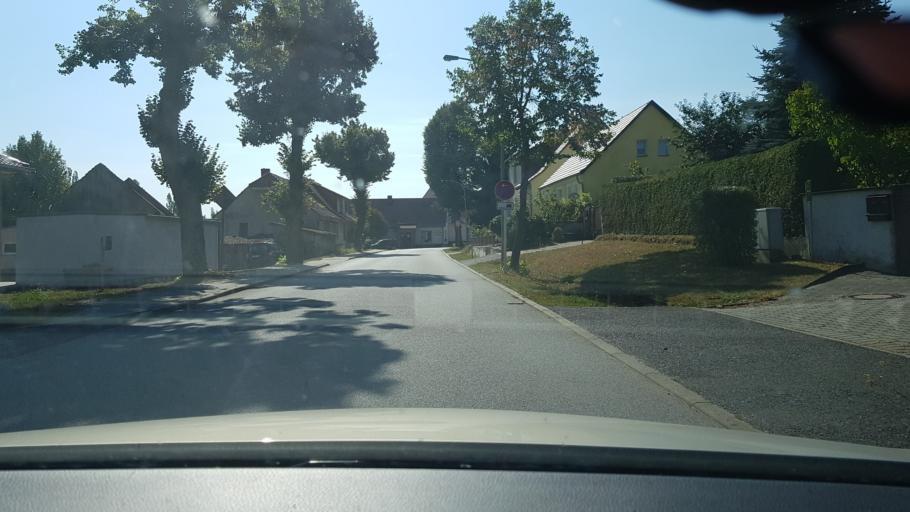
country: DE
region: Brandenburg
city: Lawitz
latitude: 52.1277
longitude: 14.5916
